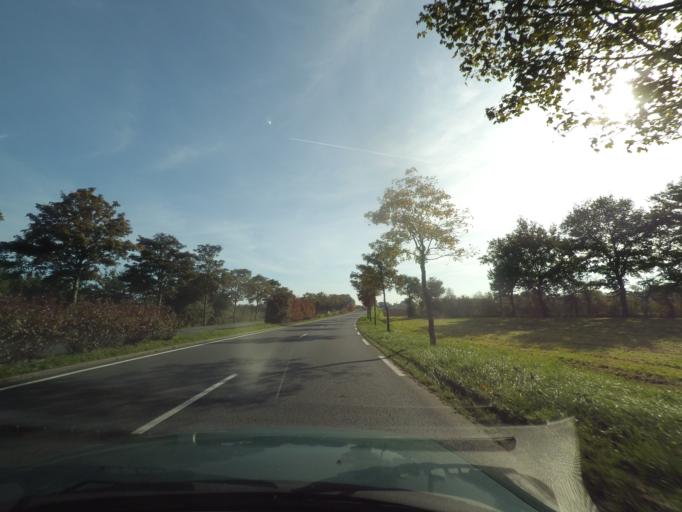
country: FR
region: Pays de la Loire
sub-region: Departement de Maine-et-Loire
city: Cholet
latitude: 47.0757
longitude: -0.8888
